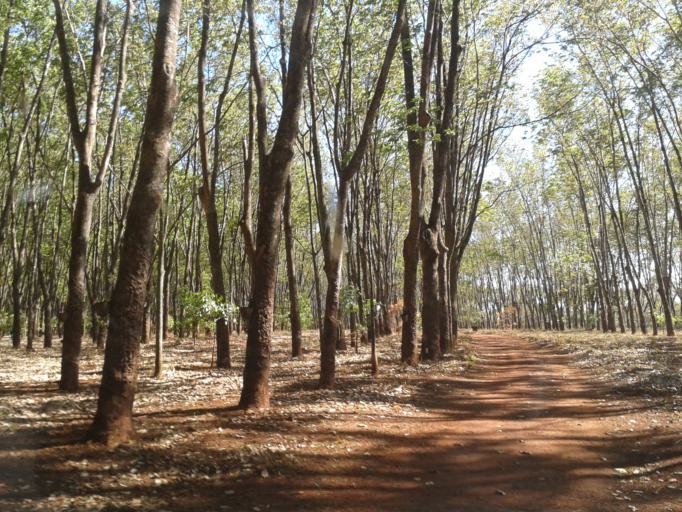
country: BR
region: Minas Gerais
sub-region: Centralina
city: Centralina
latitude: -18.5660
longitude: -49.1327
